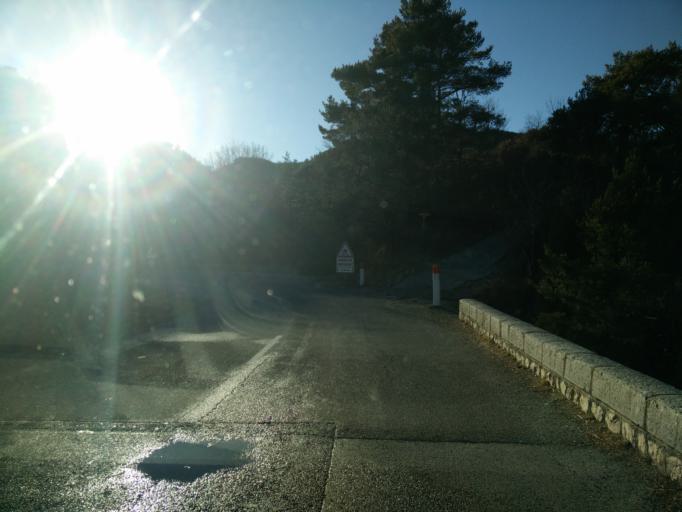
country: FR
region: Provence-Alpes-Cote d'Azur
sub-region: Departement des Alpes-de-Haute-Provence
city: Castellane
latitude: 43.7921
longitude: 6.3780
